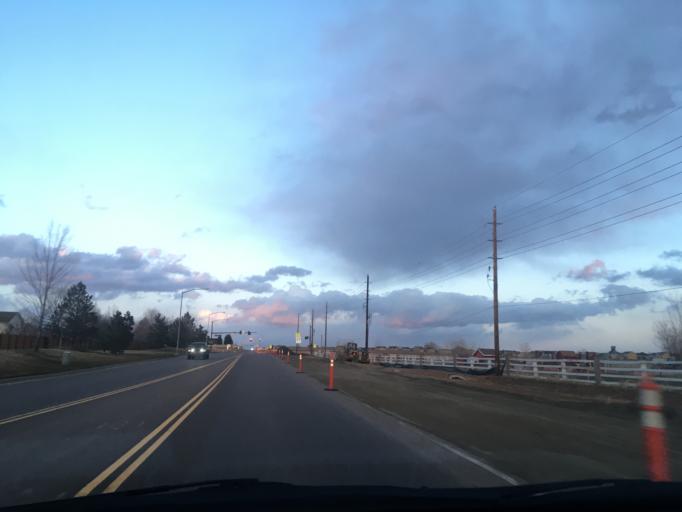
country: US
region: Colorado
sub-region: Adams County
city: Northglenn
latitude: 39.9575
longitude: -104.9621
